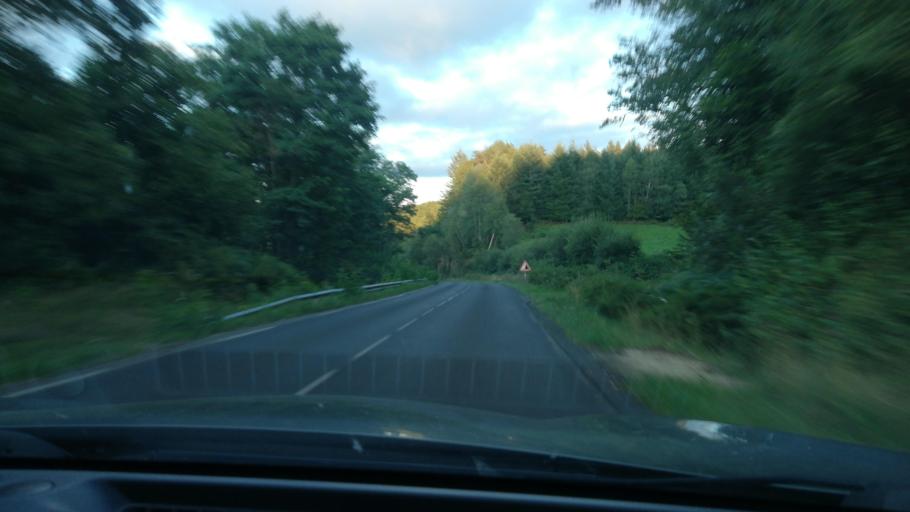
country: FR
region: Auvergne
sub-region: Departement du Cantal
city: Laroquebrou
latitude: 44.9603
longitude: 2.1661
